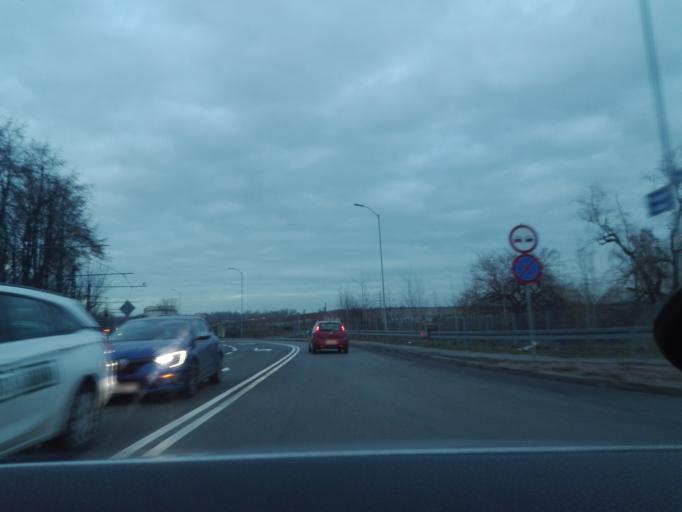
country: PL
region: Silesian Voivodeship
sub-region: Katowice
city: Katowice
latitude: 50.2802
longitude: 19.0211
